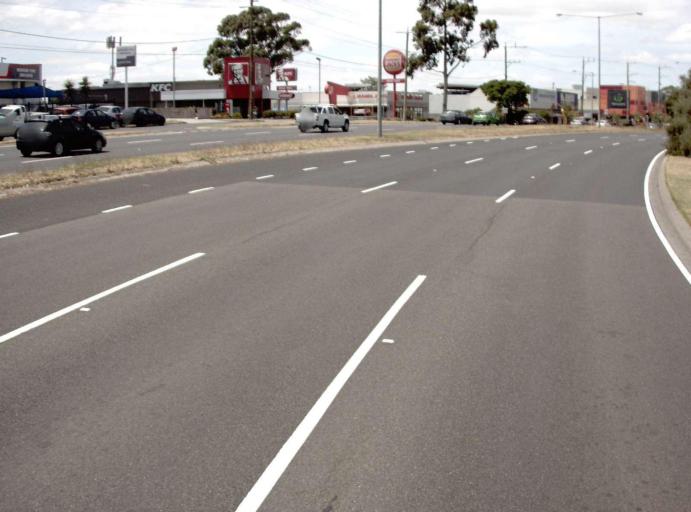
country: AU
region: Victoria
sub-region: Kingston
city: Mentone
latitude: -37.9828
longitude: 145.0745
